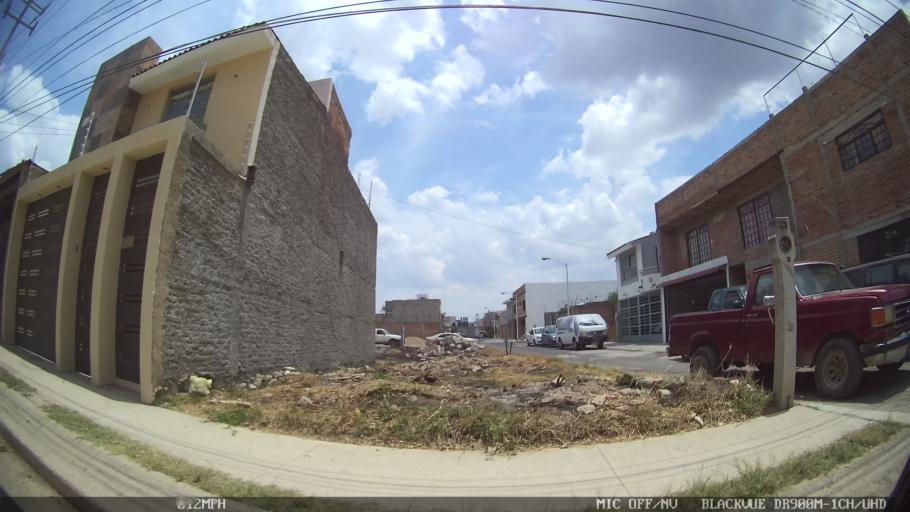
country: MX
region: Jalisco
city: Coyula
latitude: 20.6622
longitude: -103.2217
